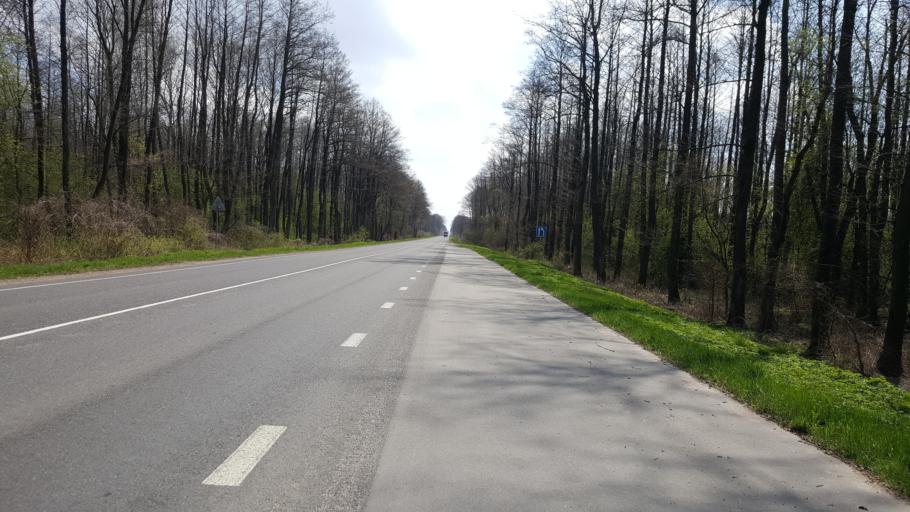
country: BY
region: Brest
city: Zhabinka
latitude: 52.2850
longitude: 23.9451
